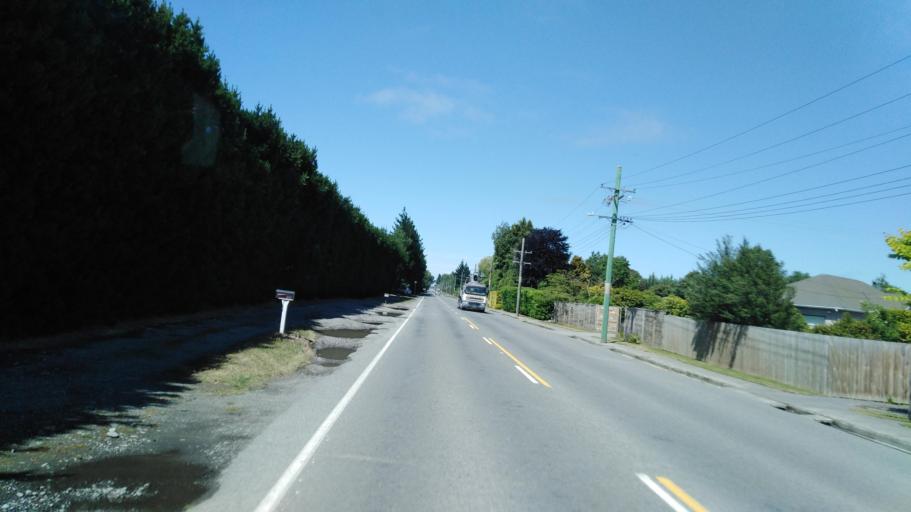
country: NZ
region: Canterbury
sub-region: Selwyn District
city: Prebbleton
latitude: -43.5140
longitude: 172.5081
